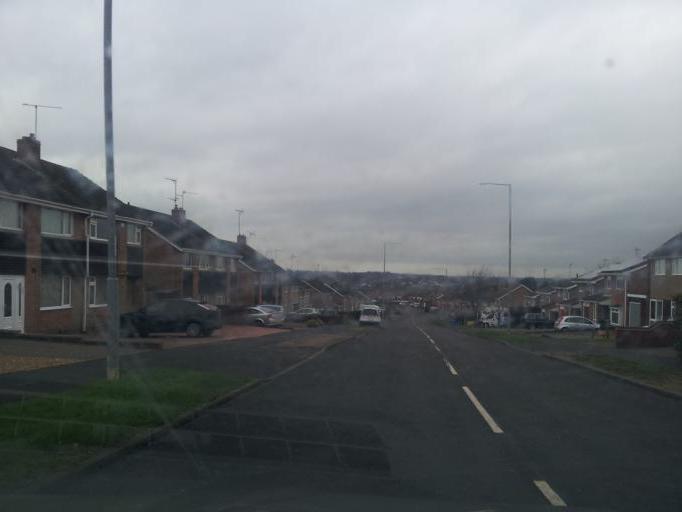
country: GB
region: England
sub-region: Northamptonshire
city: Burton Latimer
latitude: 52.3941
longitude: -0.6920
